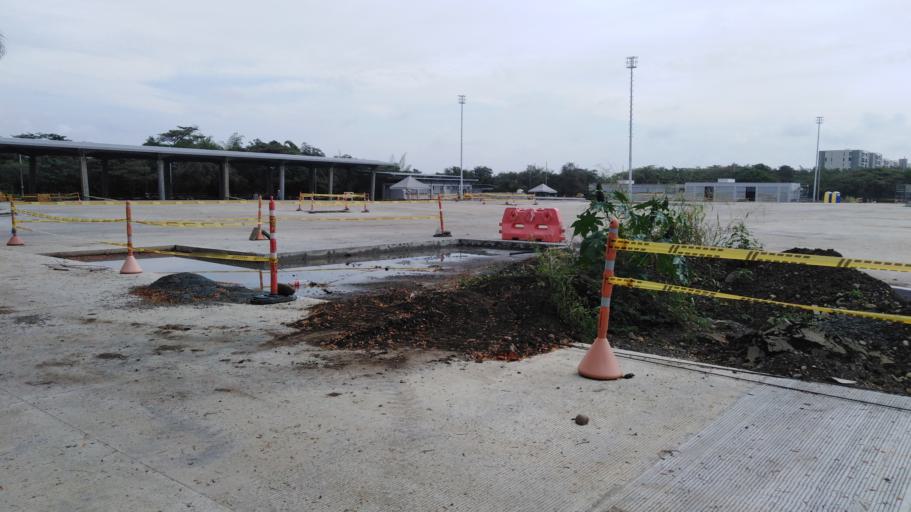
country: CO
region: Valle del Cauca
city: Cali
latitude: 3.3598
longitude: -76.5224
